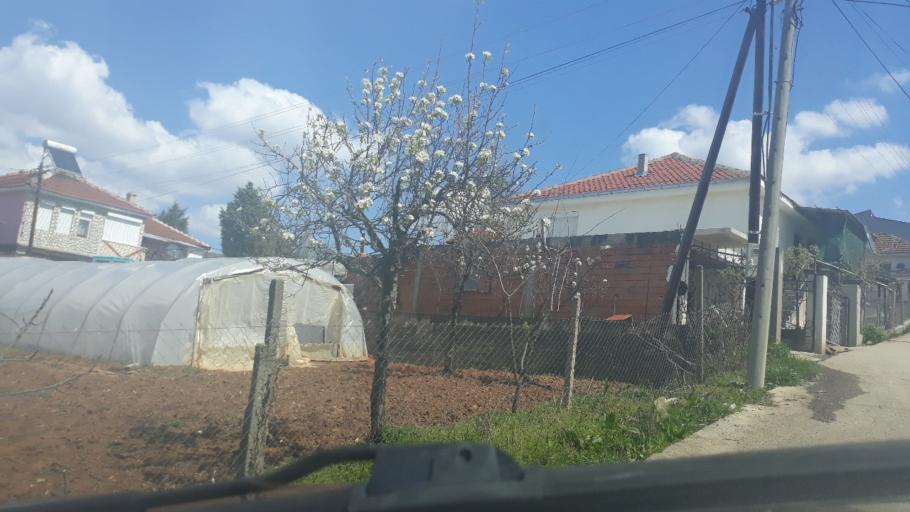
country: MK
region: Caska
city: Caska
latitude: 41.6504
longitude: 21.6947
